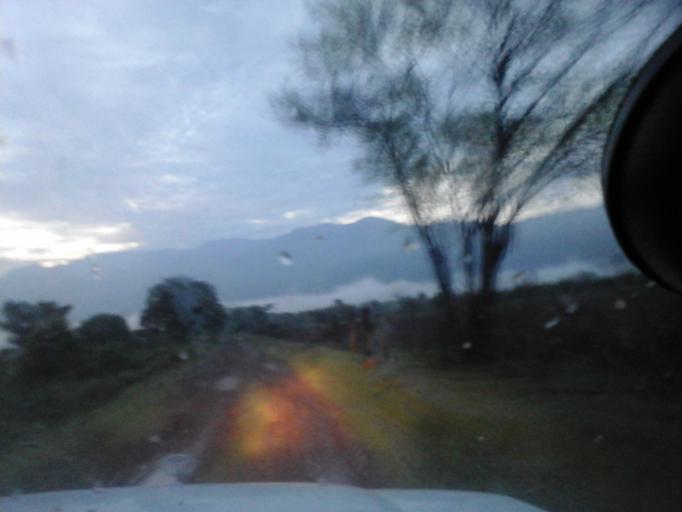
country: CO
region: Cesar
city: Agustin Codazzi
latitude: 10.1550
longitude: -73.2191
